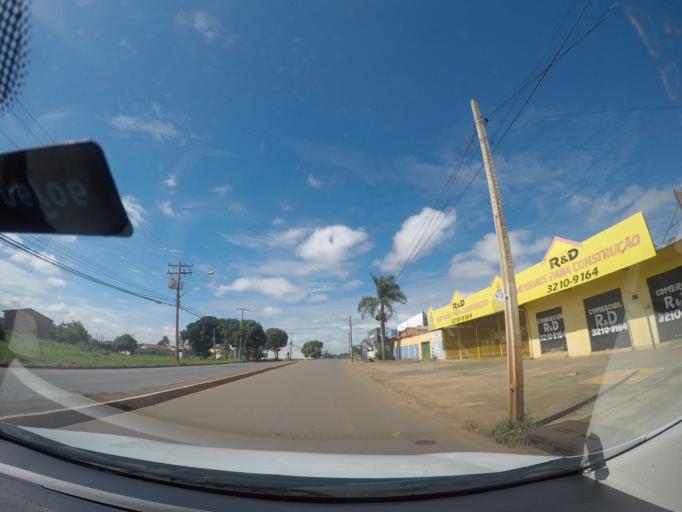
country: BR
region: Goias
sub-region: Goiania
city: Goiania
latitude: -16.6257
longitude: -49.2843
